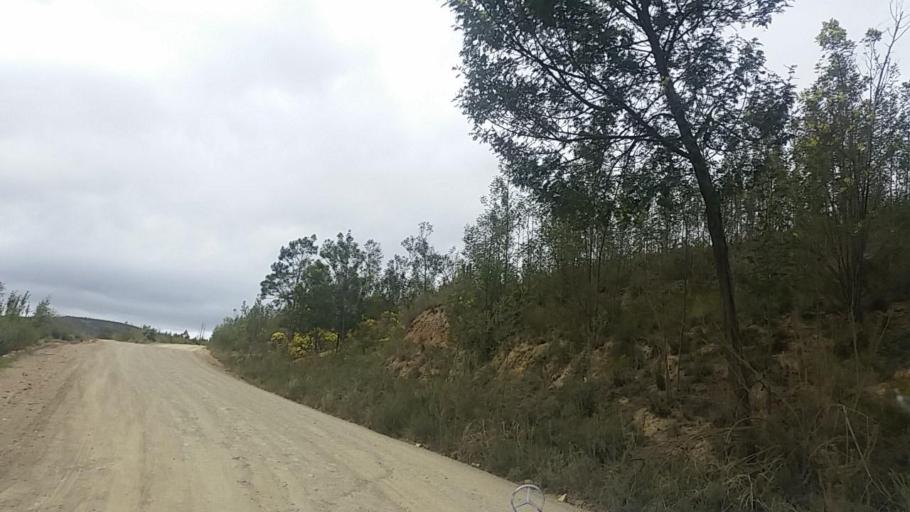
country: ZA
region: Western Cape
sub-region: Eden District Municipality
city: Knysna
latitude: -33.7522
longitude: 23.1678
